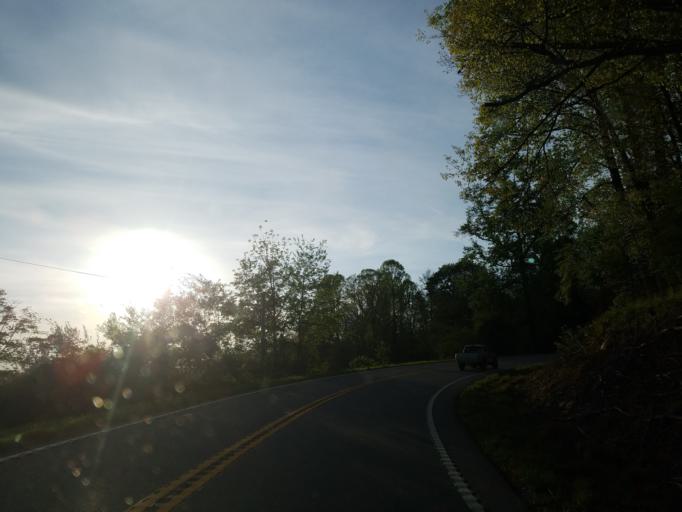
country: US
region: Georgia
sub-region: Fannin County
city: Blue Ridge
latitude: 34.8386
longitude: -84.1908
